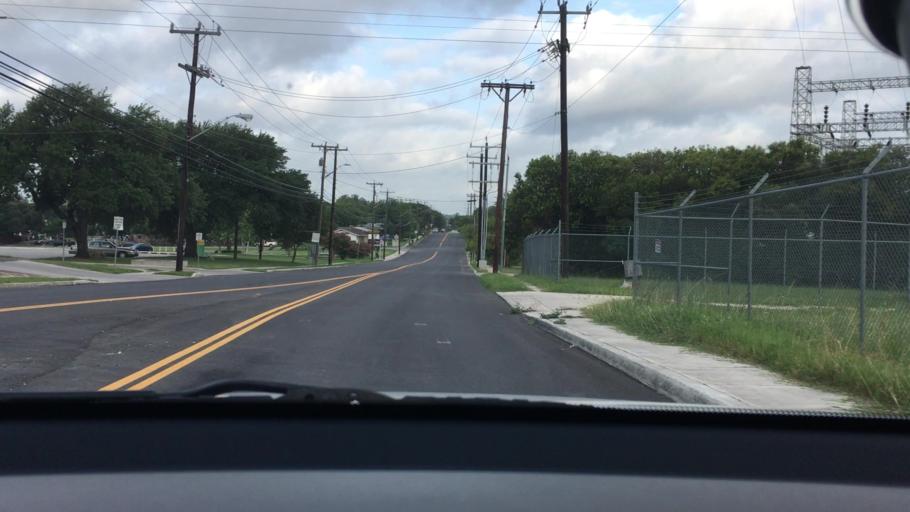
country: US
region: Texas
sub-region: Bexar County
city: Windcrest
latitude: 29.5034
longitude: -98.4074
